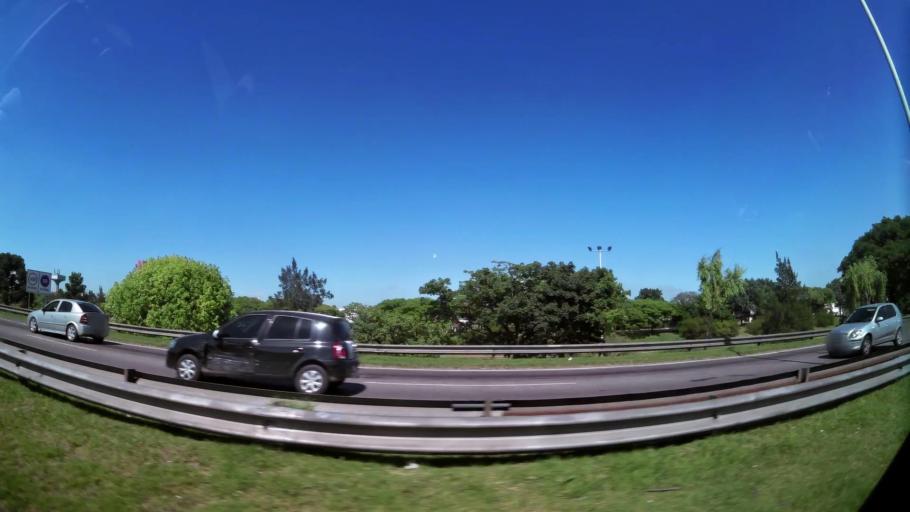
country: AR
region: Buenos Aires
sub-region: Partido de Tigre
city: Tigre
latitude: -34.4679
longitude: -58.5688
